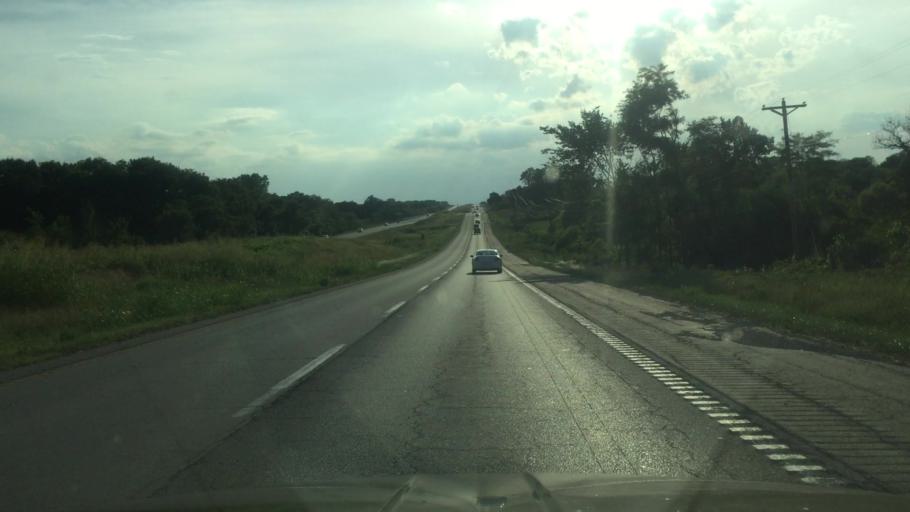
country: US
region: Missouri
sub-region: Jackson County
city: Lone Jack
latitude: 38.8702
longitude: -94.1239
